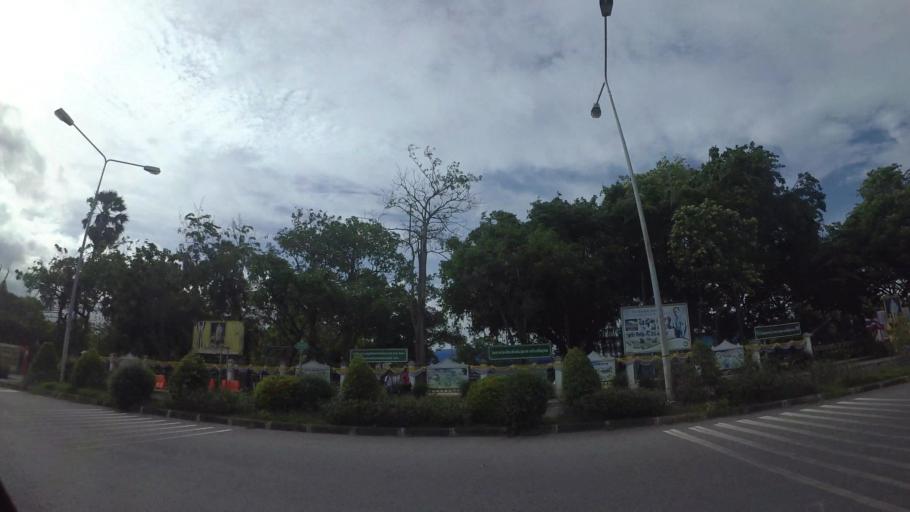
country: TH
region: Rayong
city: Rayong
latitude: 12.6638
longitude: 101.2604
